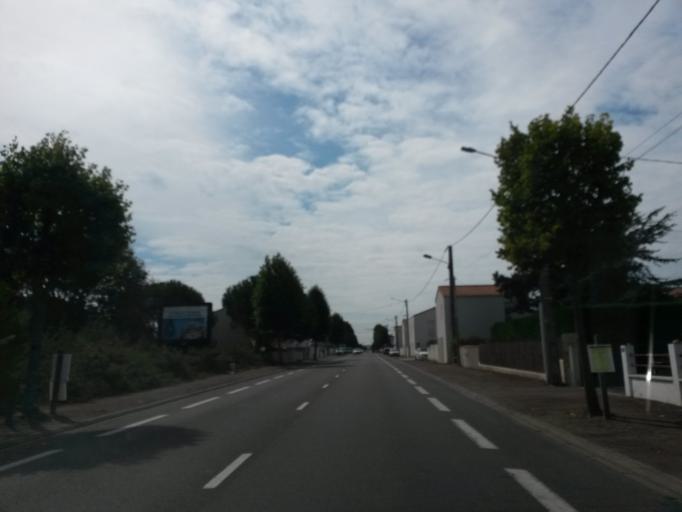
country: FR
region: Pays de la Loire
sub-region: Departement de la Vendee
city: Olonne-sur-Mer
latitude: 46.5221
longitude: -1.7754
